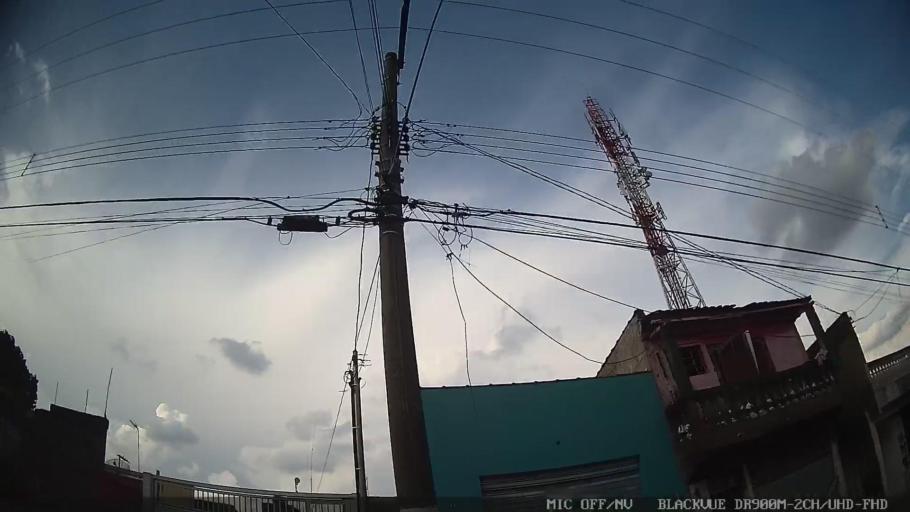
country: BR
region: Sao Paulo
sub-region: Braganca Paulista
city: Braganca Paulista
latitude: -22.9168
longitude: -46.5525
